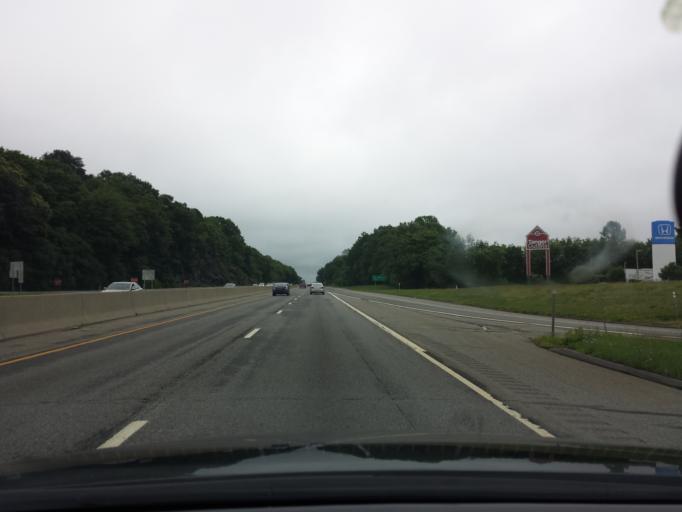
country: US
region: Connecticut
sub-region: Middlesex County
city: Westbrook Center
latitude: 41.2916
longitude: -72.4431
